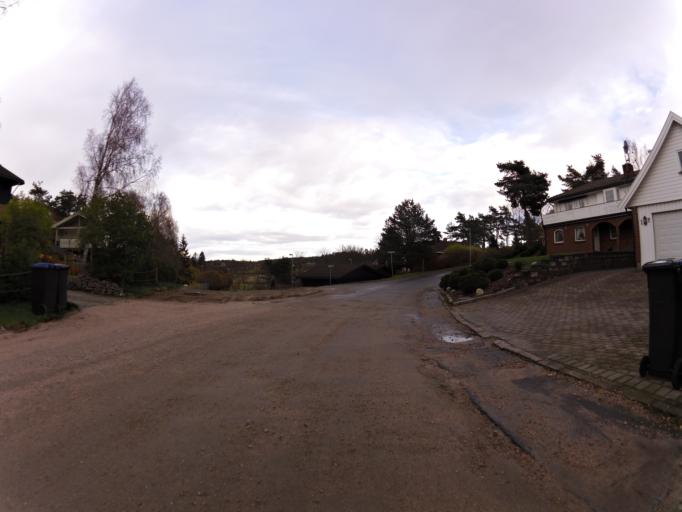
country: NO
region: Ostfold
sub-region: Fredrikstad
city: Fredrikstad
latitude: 59.2321
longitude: 10.9243
